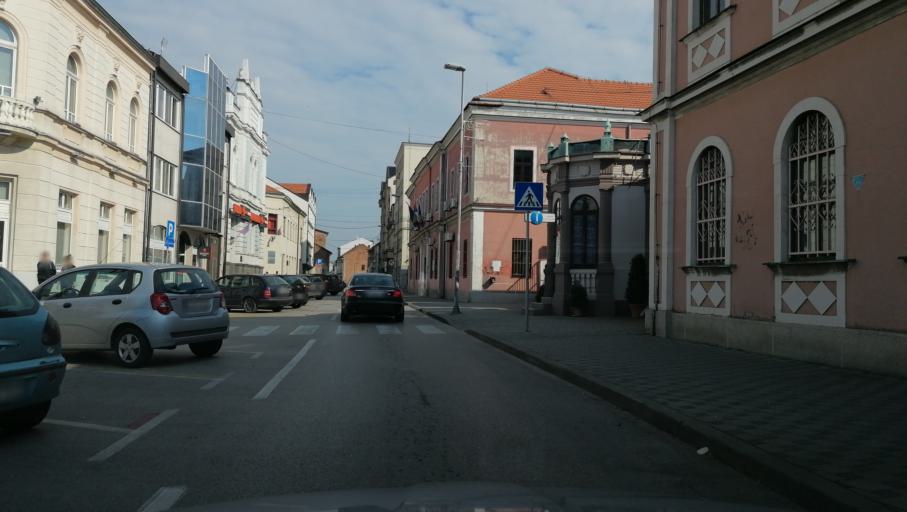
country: BA
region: Republika Srpska
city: Bijeljina
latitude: 44.7570
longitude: 19.2179
